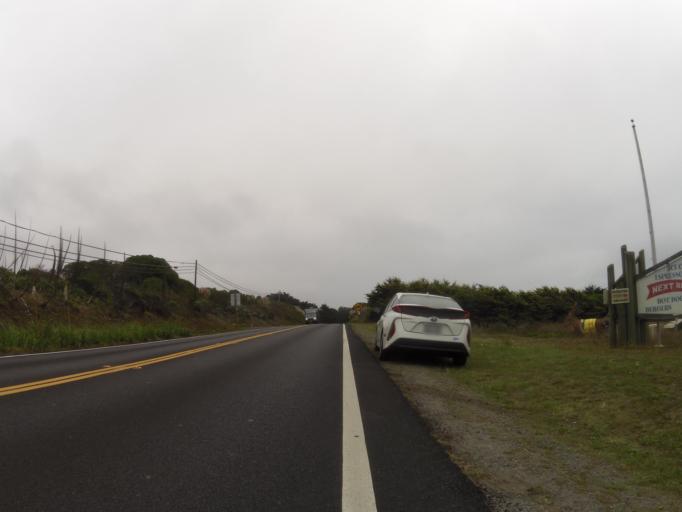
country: US
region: California
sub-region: Sonoma County
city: Bodega Bay
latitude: 38.3246
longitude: -123.0387
